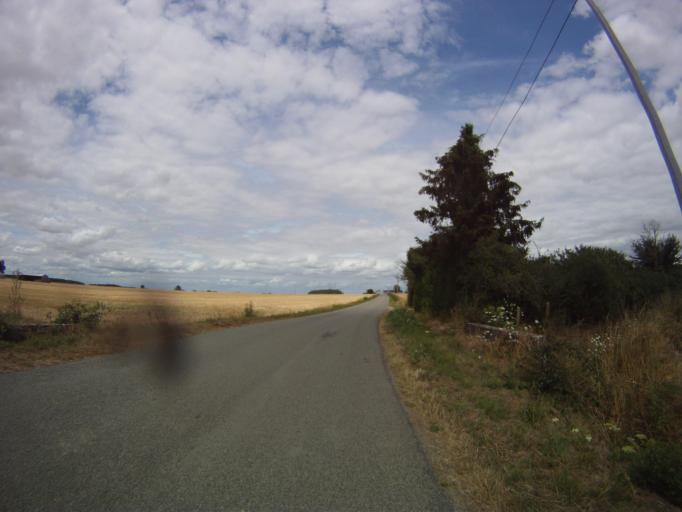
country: FR
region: Centre
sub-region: Departement du Loir-et-Cher
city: Montoire-sur-le-Loir
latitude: 47.6861
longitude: 0.8105
